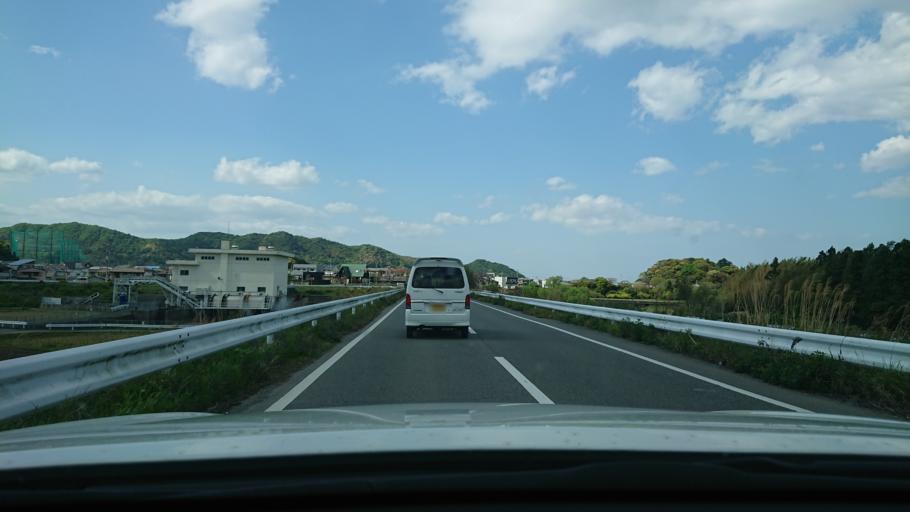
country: JP
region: Tokushima
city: Komatsushimacho
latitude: 33.9986
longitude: 134.5475
